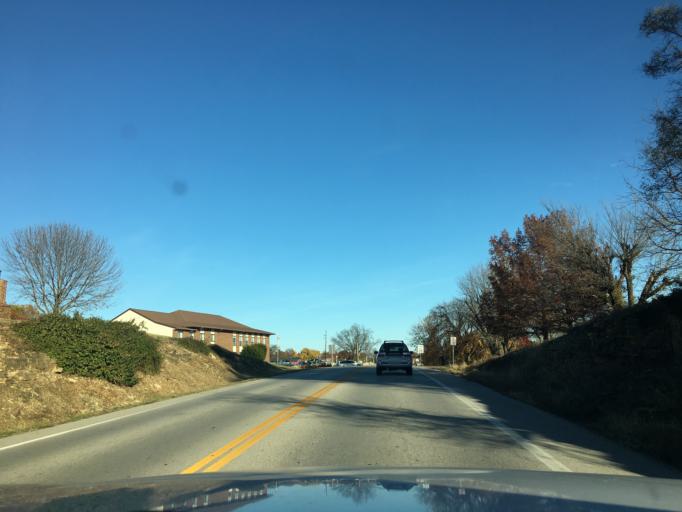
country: US
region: Missouri
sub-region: Franklin County
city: New Haven
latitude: 38.6006
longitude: -91.2280
